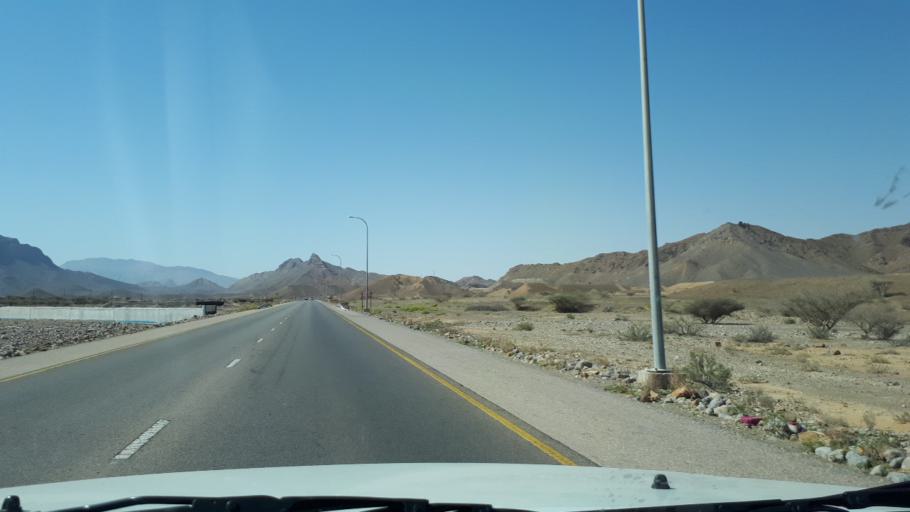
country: OM
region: Ash Sharqiyah
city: Sur
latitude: 22.3576
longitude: 59.3125
